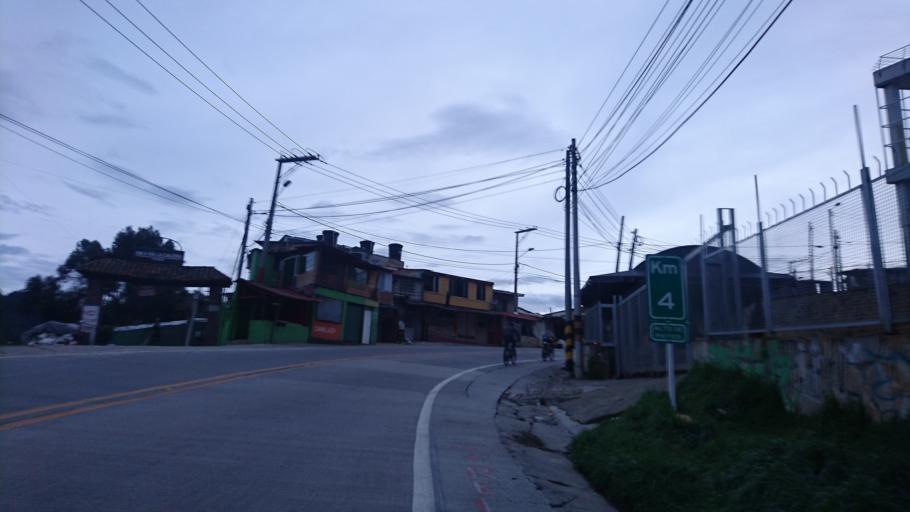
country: CO
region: Bogota D.C.
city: Barrio San Luis
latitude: 4.6755
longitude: -74.0239
